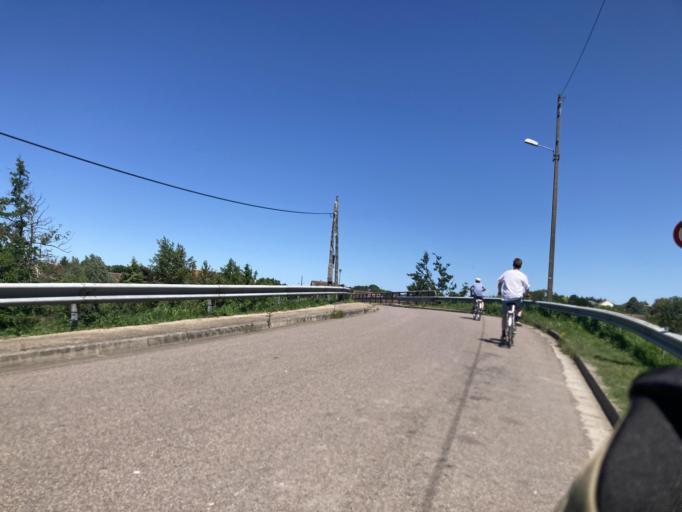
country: FR
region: Bourgogne
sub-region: Departement de l'Yonne
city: Laroche-Saint-Cydroine
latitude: 47.9620
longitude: 3.4846
